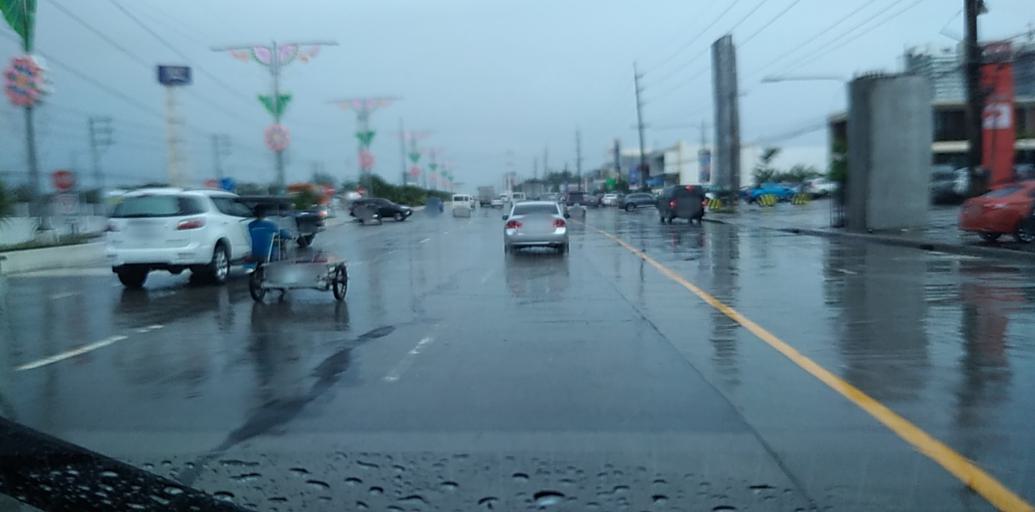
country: PH
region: Central Luzon
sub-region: Province of Pampanga
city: Del Pilar
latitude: 15.0462
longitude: 120.6906
